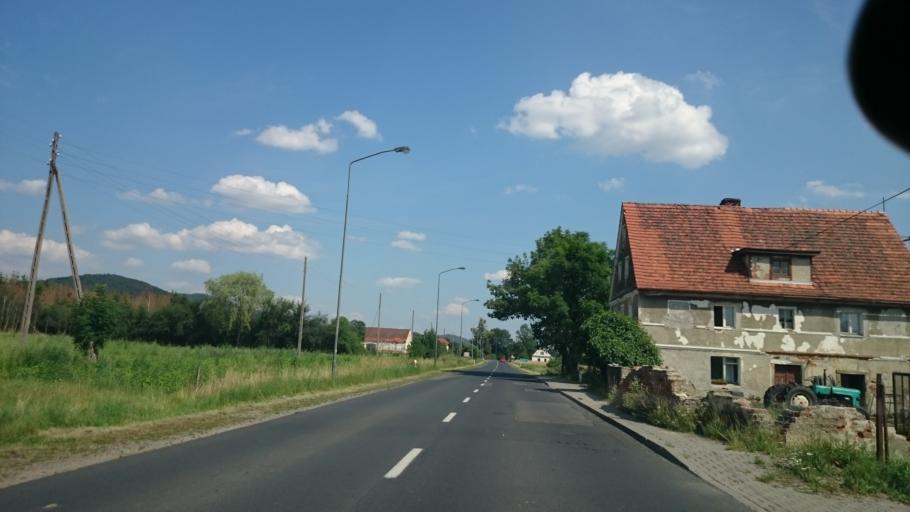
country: PL
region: Lower Silesian Voivodeship
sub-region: Powiat klodzki
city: Klodzko
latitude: 50.3687
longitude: 16.6816
